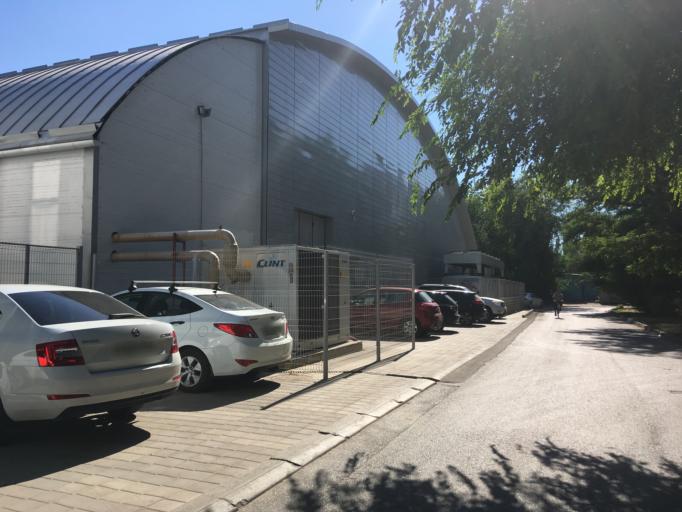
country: RU
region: Rostov
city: Rostov-na-Donu
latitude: 47.2091
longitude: 39.6275
